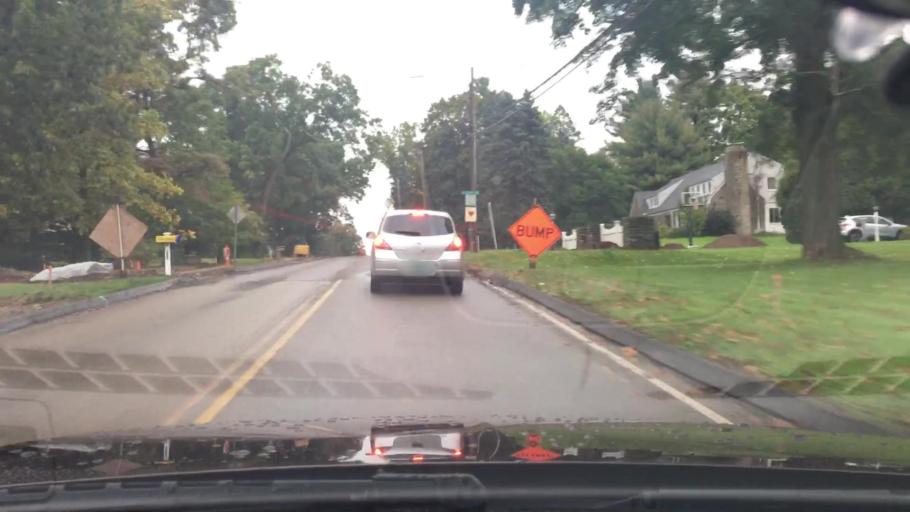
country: US
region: Connecticut
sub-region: Hartford County
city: Manchester
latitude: 41.8158
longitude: -72.5234
